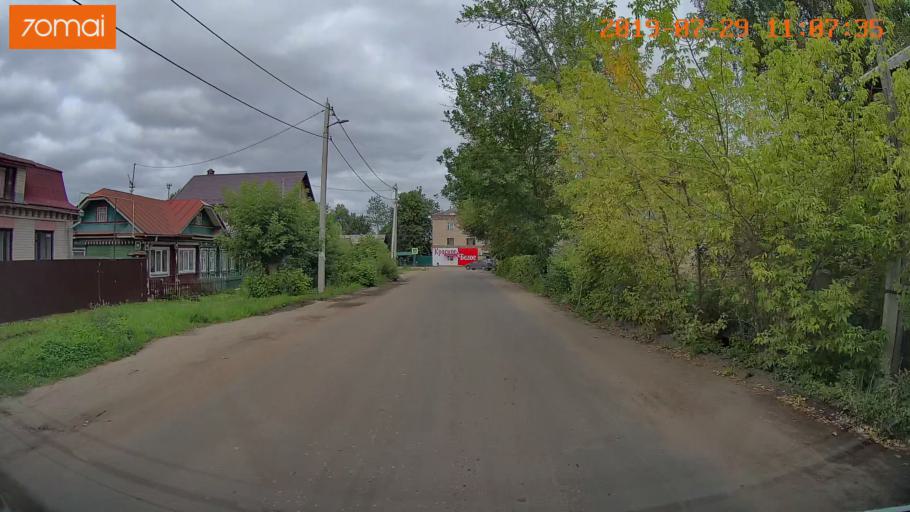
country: RU
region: Ivanovo
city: Bogorodskoye
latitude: 56.9948
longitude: 41.0372
